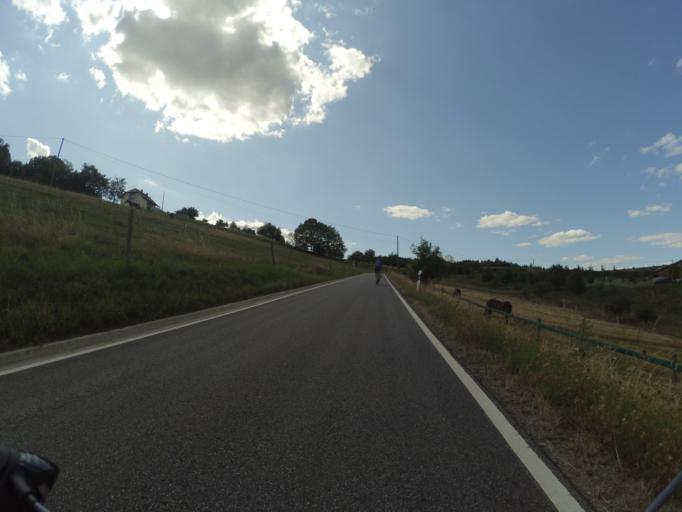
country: DE
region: Rheinland-Pfalz
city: Bescheid
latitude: 49.7612
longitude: 6.8807
